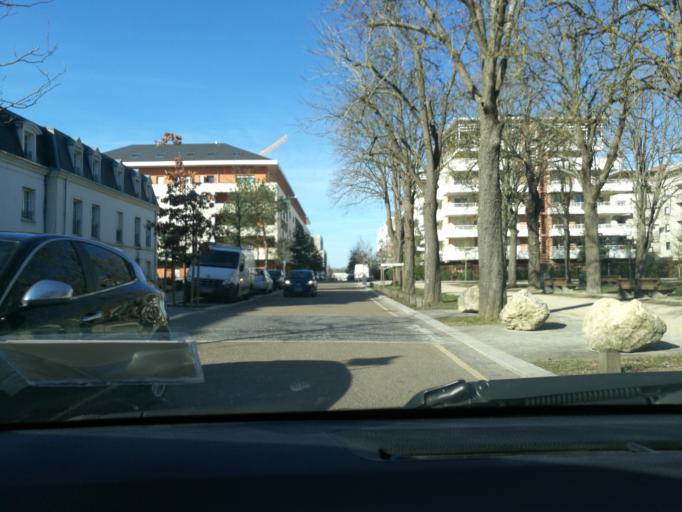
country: FR
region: Centre
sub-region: Departement du Loiret
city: Orleans
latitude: 47.9088
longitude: 1.8897
